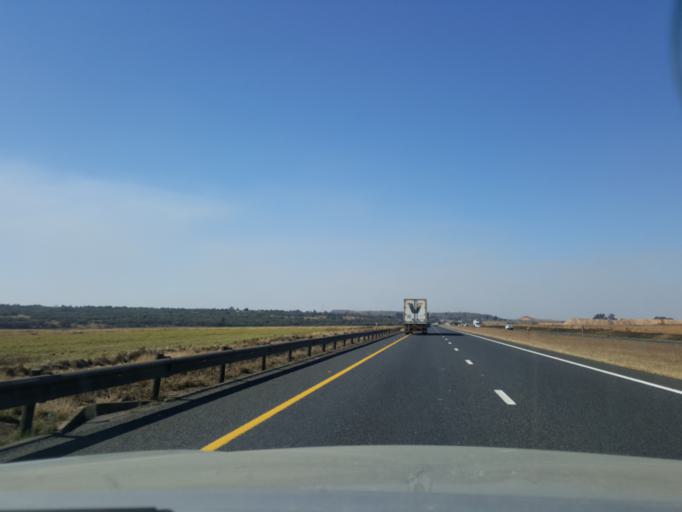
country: ZA
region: Mpumalanga
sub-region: Nkangala District Municipality
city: Delmas
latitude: -26.0186
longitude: 28.9326
